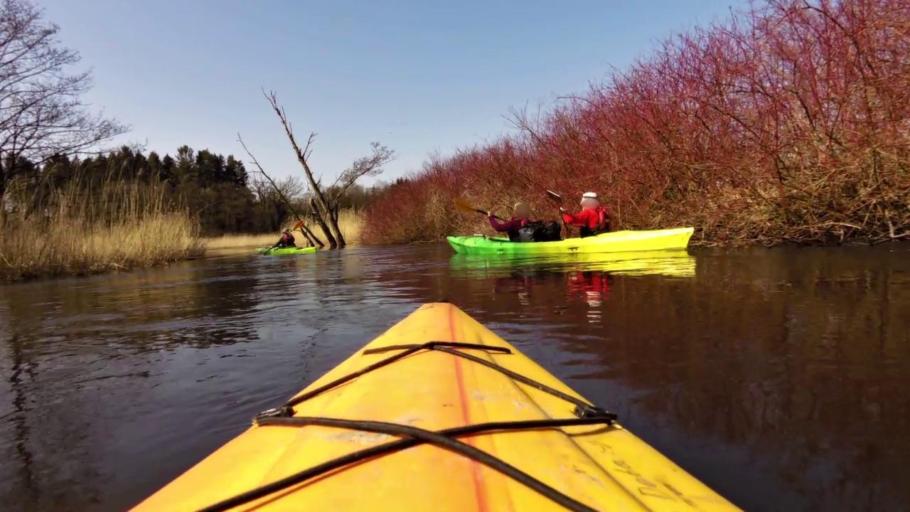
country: PL
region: West Pomeranian Voivodeship
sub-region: Powiat lobeski
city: Radowo Male
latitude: 53.7426
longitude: 15.5225
